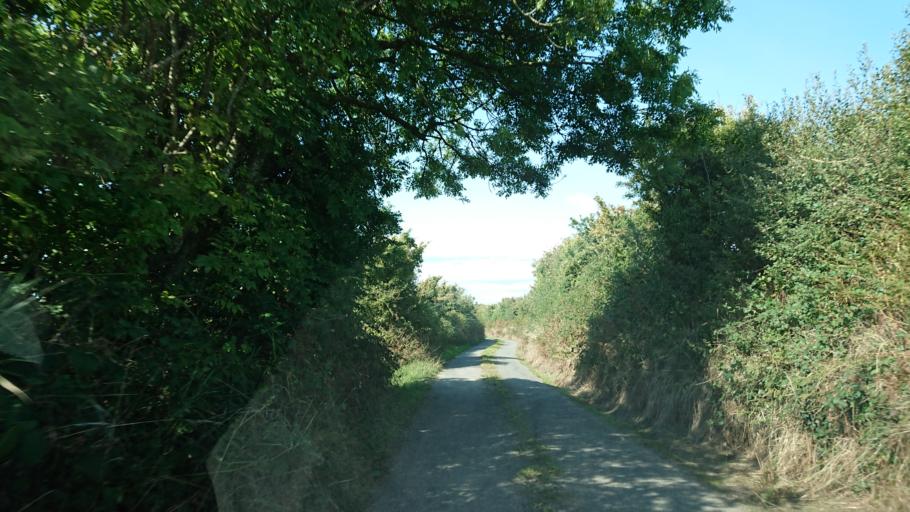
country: IE
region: Munster
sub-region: Waterford
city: Waterford
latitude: 52.1994
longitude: -7.0598
